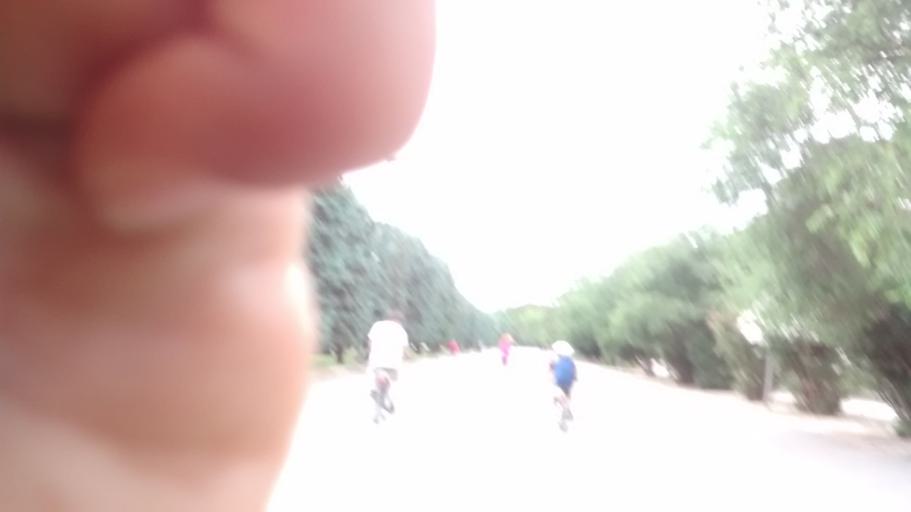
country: ES
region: Aragon
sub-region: Provincia de Zaragoza
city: Delicias
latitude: 41.6347
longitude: -0.8942
